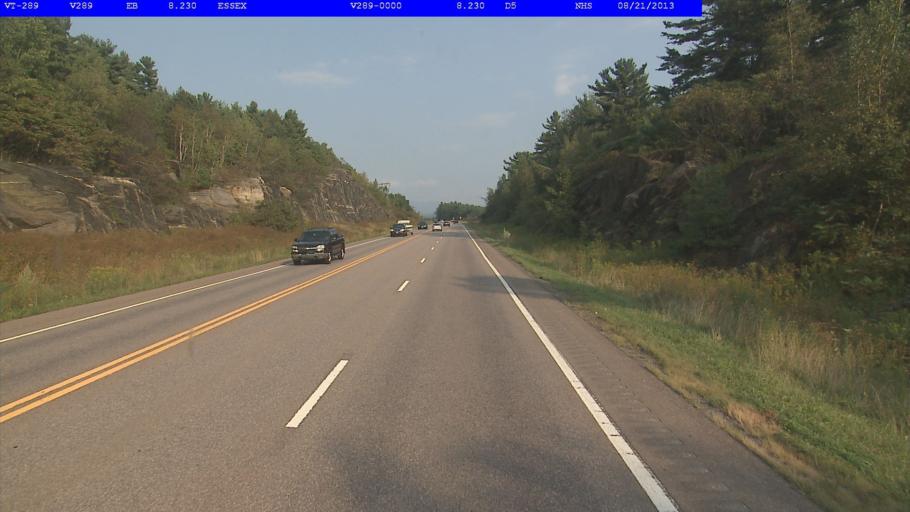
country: US
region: Vermont
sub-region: Chittenden County
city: Essex Junction
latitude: 44.5160
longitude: -73.1092
